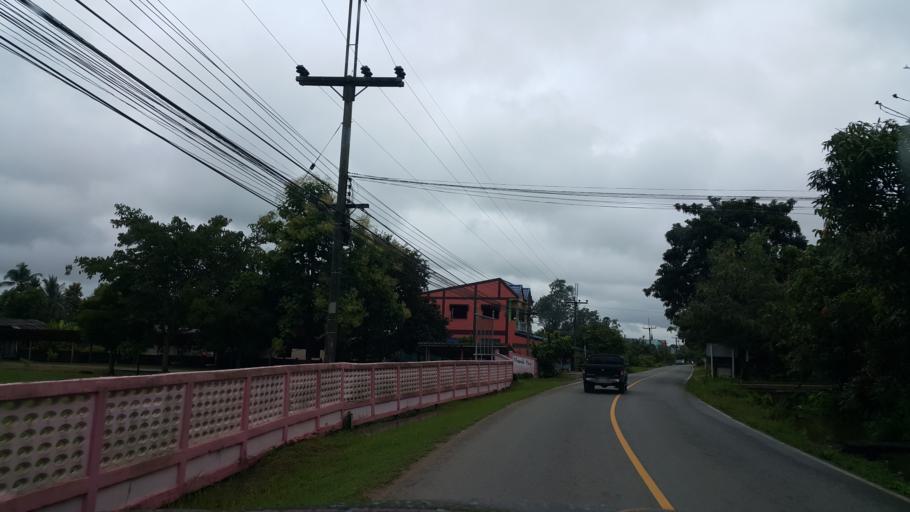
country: TH
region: Phayao
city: Chiang Kham
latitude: 19.5230
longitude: 100.3477
